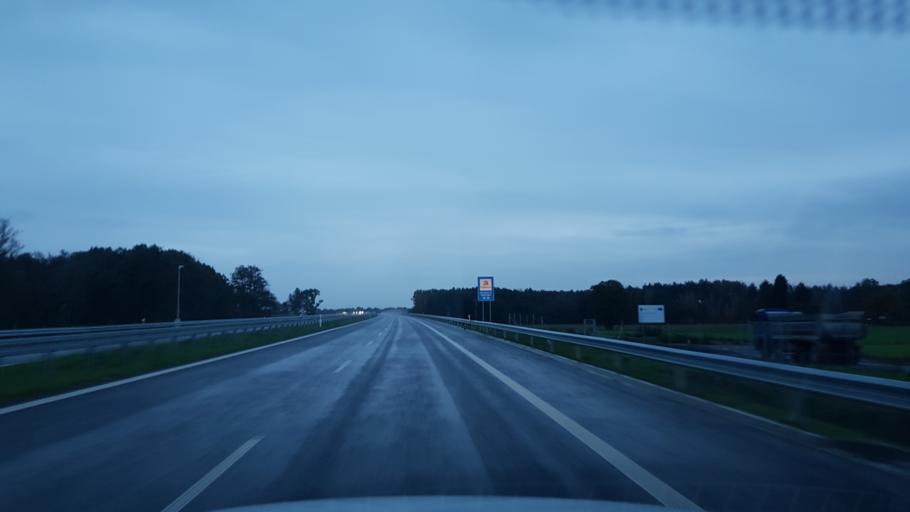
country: PL
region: West Pomeranian Voivodeship
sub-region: Powiat gryficki
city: Brojce
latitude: 53.9549
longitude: 15.4140
